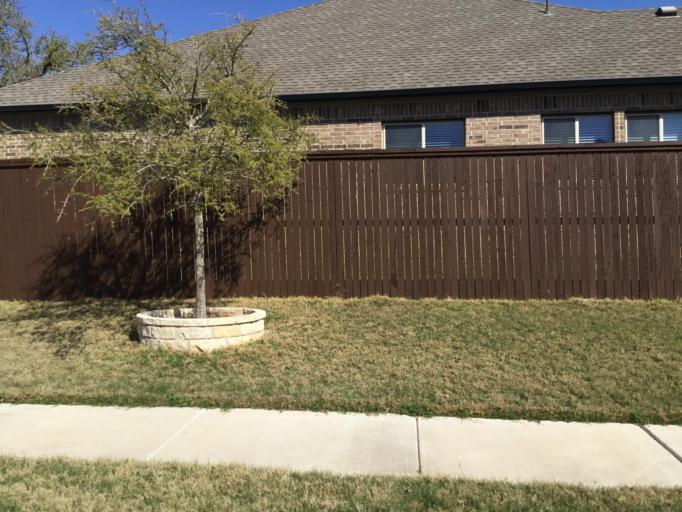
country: US
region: Texas
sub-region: Williamson County
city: Brushy Creek
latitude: 30.5736
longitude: -97.7689
